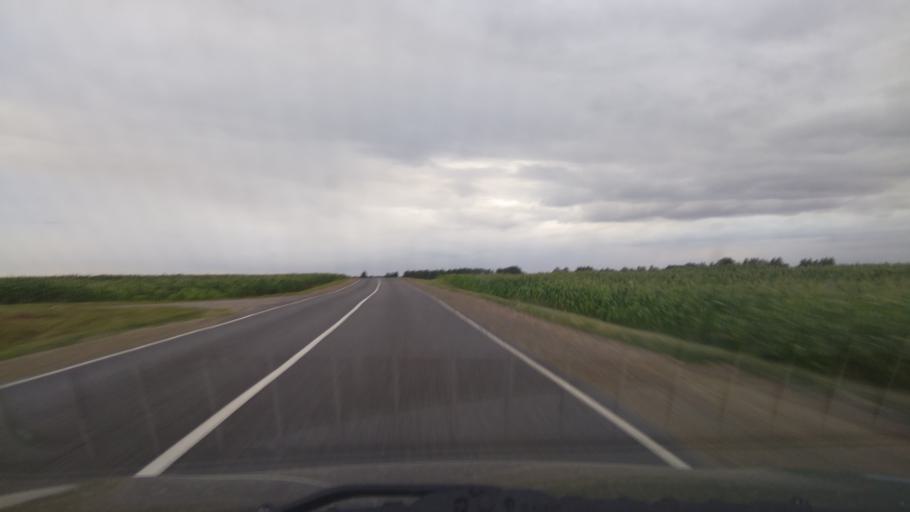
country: BY
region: Brest
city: Byaroza
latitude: 52.4320
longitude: 24.9805
